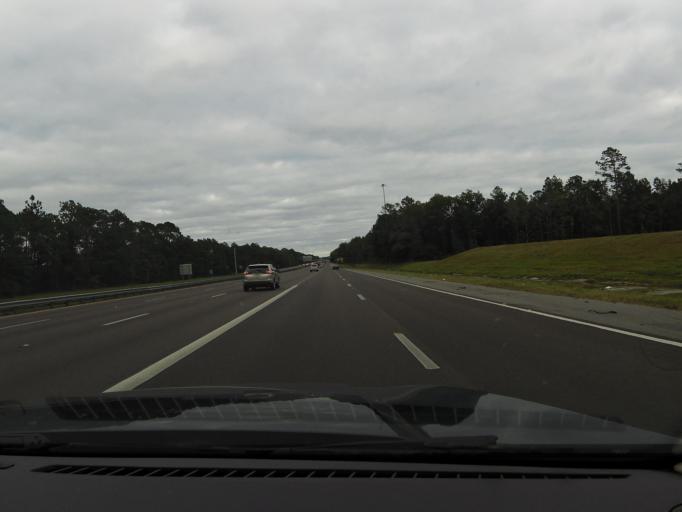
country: US
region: Florida
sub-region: Duval County
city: Baldwin
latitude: 30.3074
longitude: -81.8628
